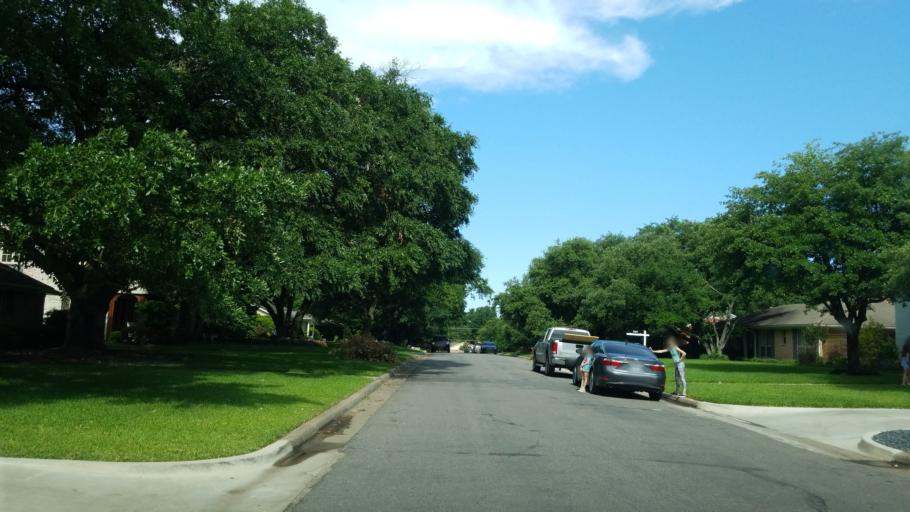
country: US
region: Texas
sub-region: Dallas County
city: Addison
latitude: 32.9043
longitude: -96.8360
